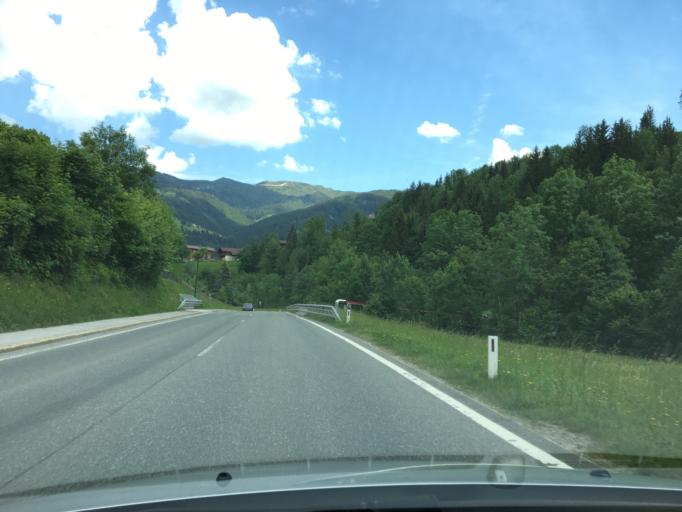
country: AT
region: Salzburg
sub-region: Politischer Bezirk Sankt Johann im Pongau
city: Wagrain
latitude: 47.3353
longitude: 13.2864
